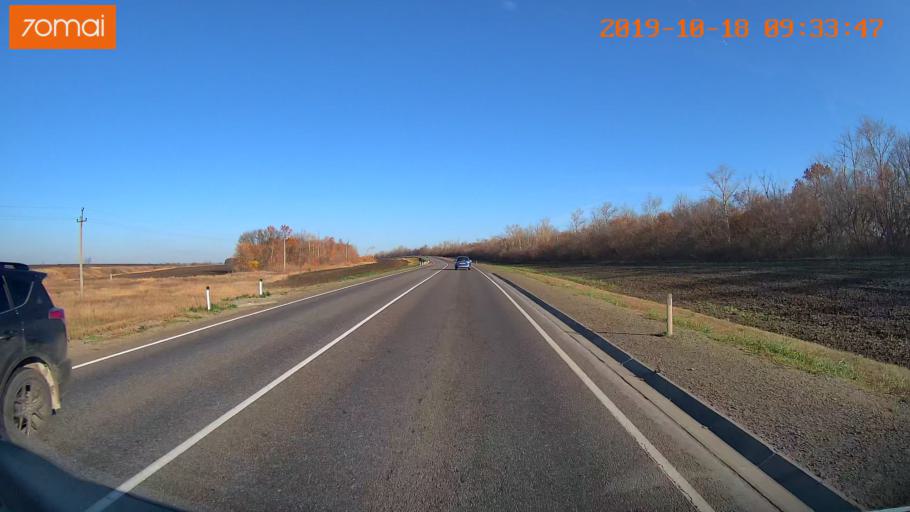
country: RU
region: Tula
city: Yefremov
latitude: 53.1714
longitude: 38.1521
